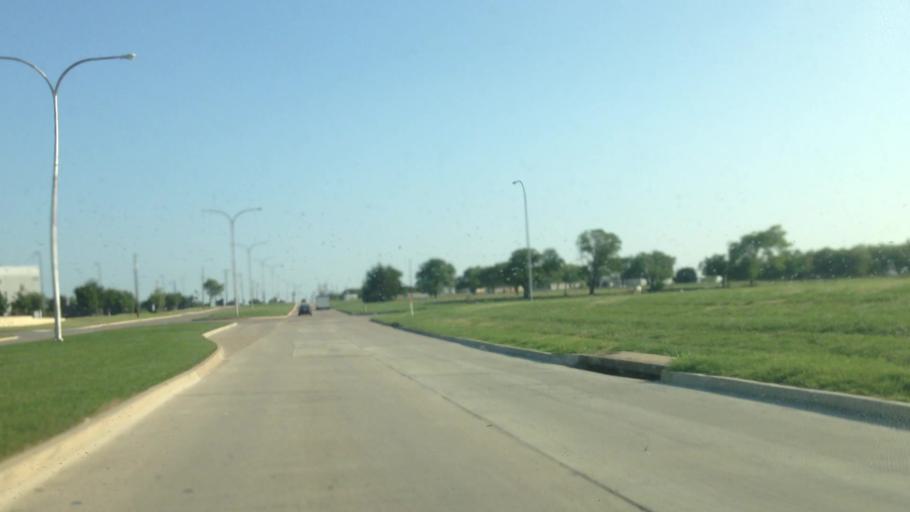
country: US
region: Texas
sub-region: Tarrant County
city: Haltom City
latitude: 32.8167
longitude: -97.3084
